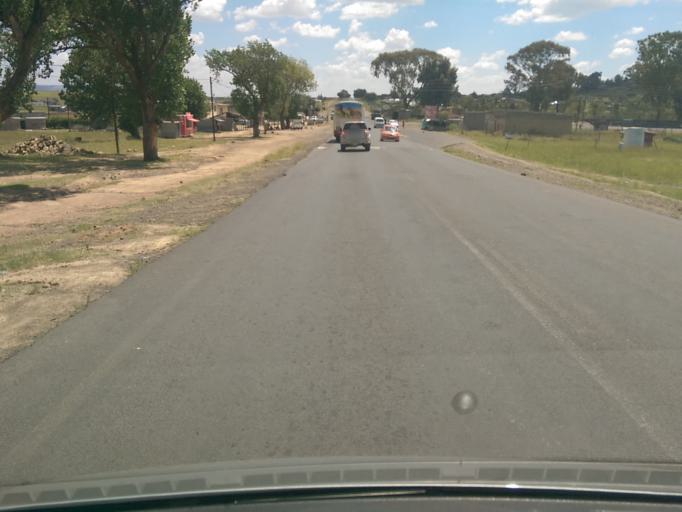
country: LS
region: Maseru
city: Maseru
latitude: -29.4114
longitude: 27.6213
